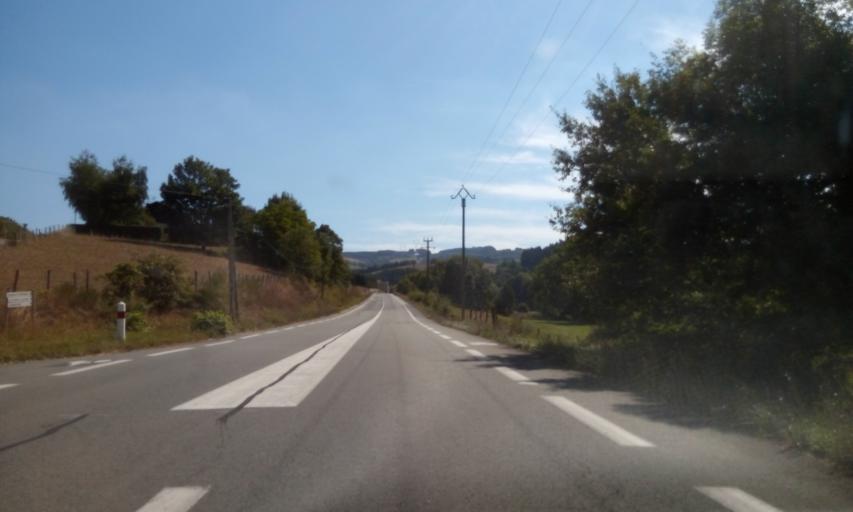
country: FR
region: Rhone-Alpes
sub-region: Departement du Rhone
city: Amplepuis
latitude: 45.9735
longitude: 4.3441
